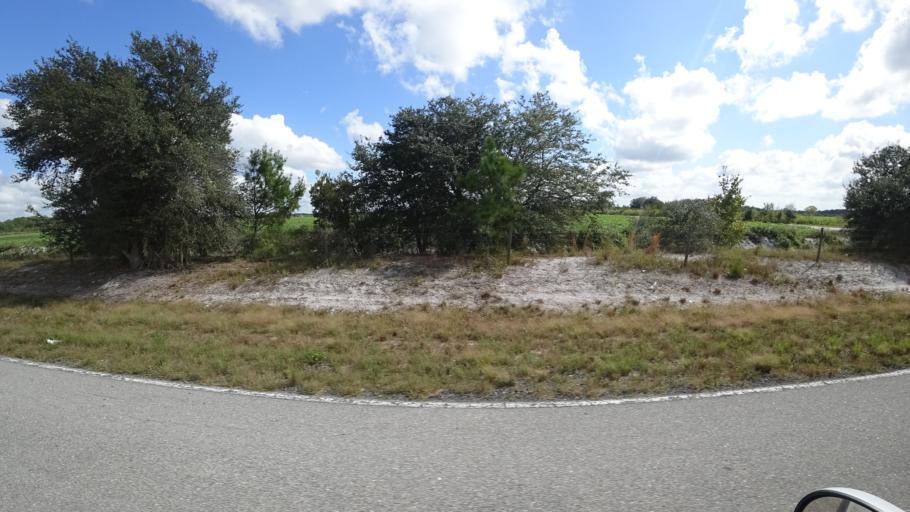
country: US
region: Florida
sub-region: Sarasota County
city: Lake Sarasota
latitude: 27.4211
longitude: -82.1332
